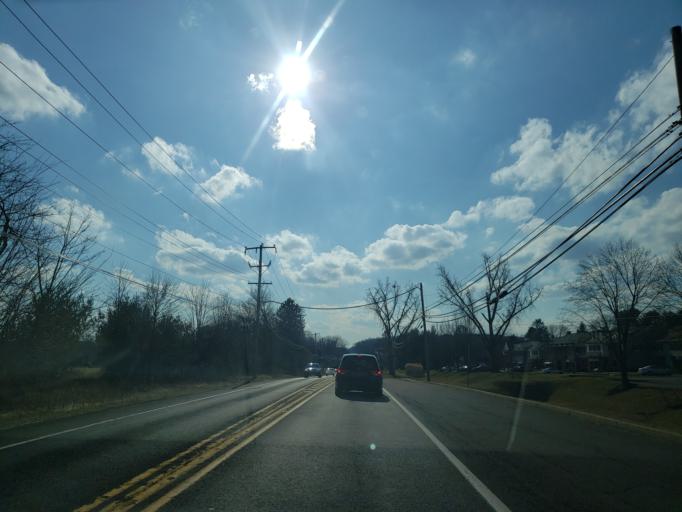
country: US
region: Pennsylvania
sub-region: Bucks County
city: Doylestown
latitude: 40.3302
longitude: -75.0536
